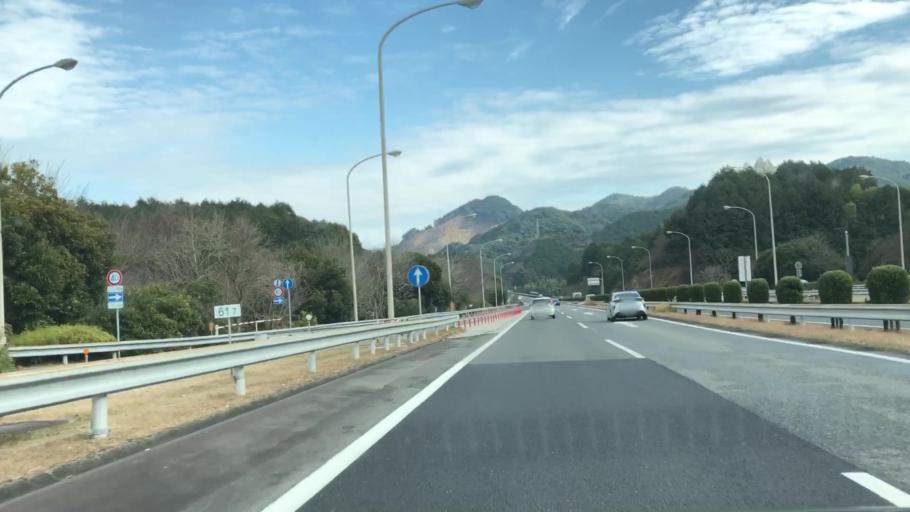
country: JP
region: Saga Prefecture
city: Takeocho-takeo
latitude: 33.1605
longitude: 130.0182
